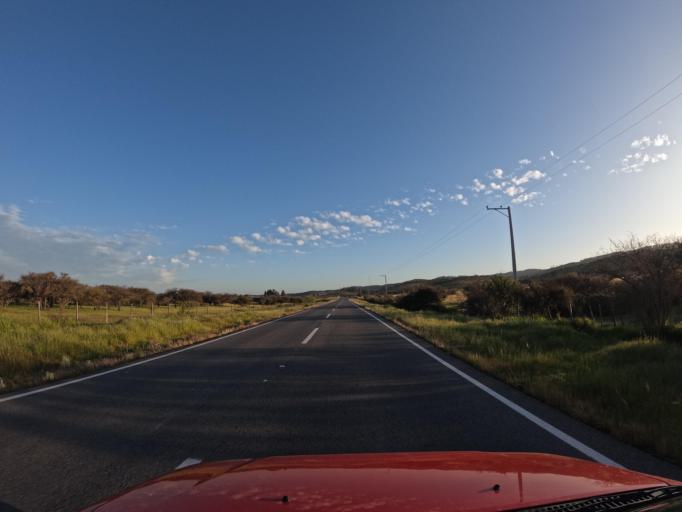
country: CL
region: O'Higgins
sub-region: Provincia de Colchagua
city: Santa Cruz
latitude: -34.3216
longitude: -71.7437
